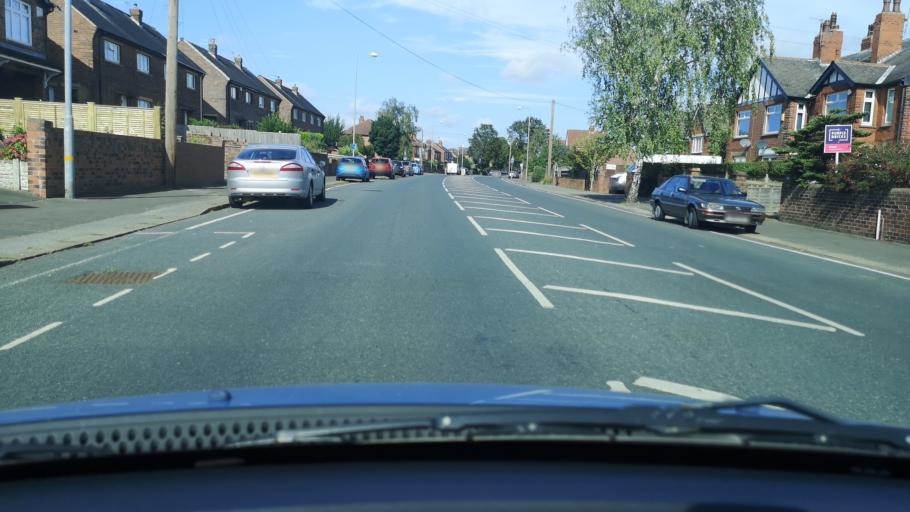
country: GB
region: England
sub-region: City and Borough of Wakefield
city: Ossett
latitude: 53.6825
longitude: -1.5860
